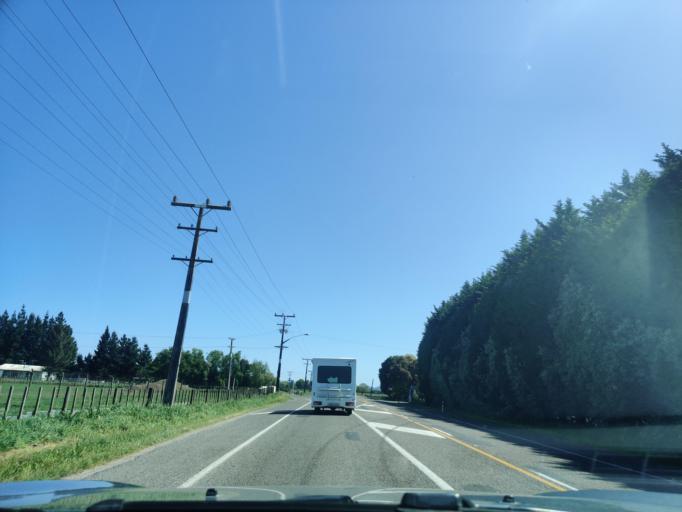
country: NZ
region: Manawatu-Wanganui
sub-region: Wanganui District
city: Wanganui
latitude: -39.8770
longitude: 174.9990
